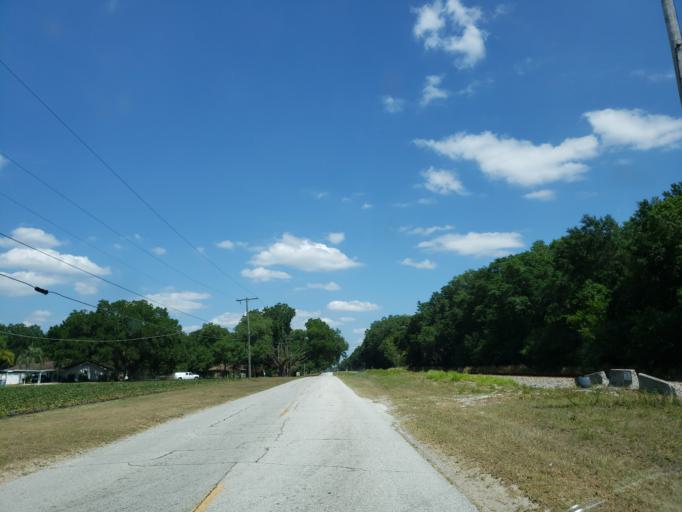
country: US
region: Florida
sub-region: Hillsborough County
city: Dover
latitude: 27.9615
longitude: -82.2124
